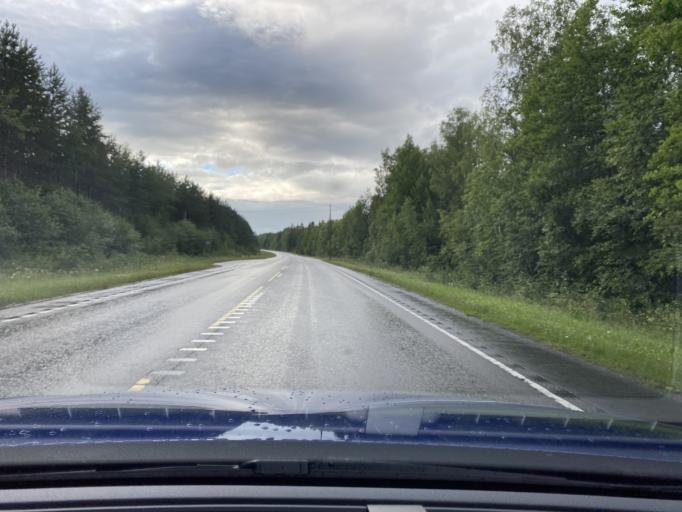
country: FI
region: Uusimaa
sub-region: Helsinki
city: Hyvinge
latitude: 60.6430
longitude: 24.8095
